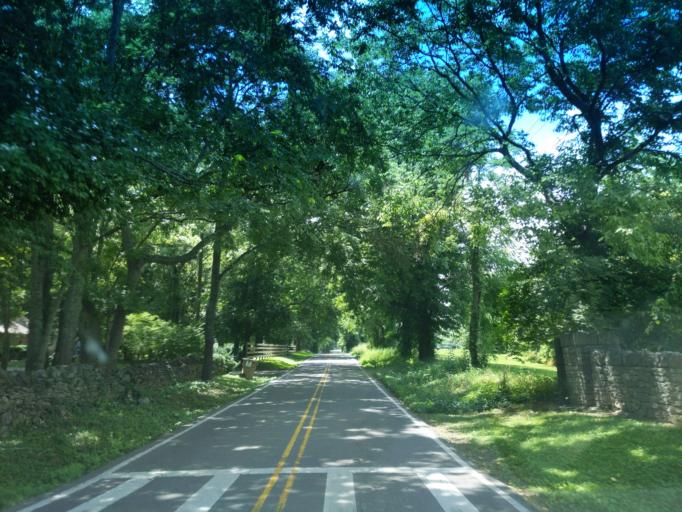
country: US
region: Tennessee
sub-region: Williamson County
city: Brentwood Estates
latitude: 36.0178
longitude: -86.7661
